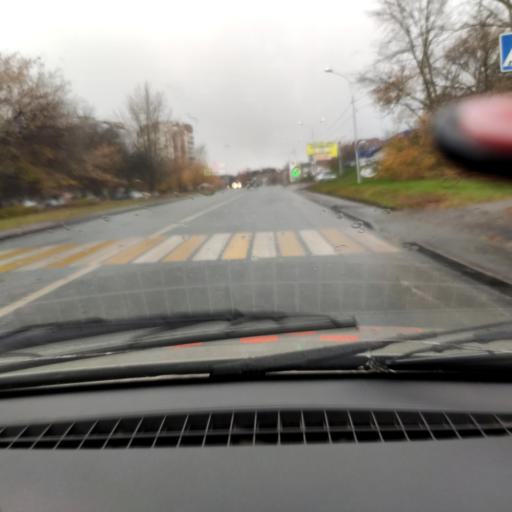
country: RU
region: Bashkortostan
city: Ufa
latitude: 54.7823
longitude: 56.0411
